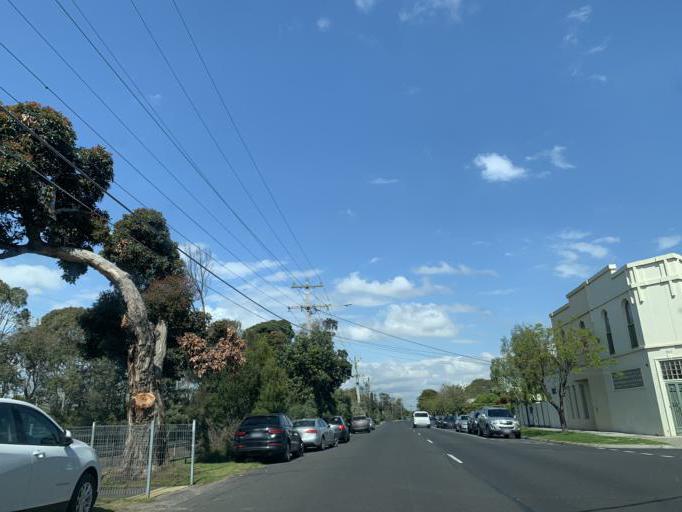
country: AU
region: Victoria
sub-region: Kingston
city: Parkdale
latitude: -37.9956
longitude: 145.0789
